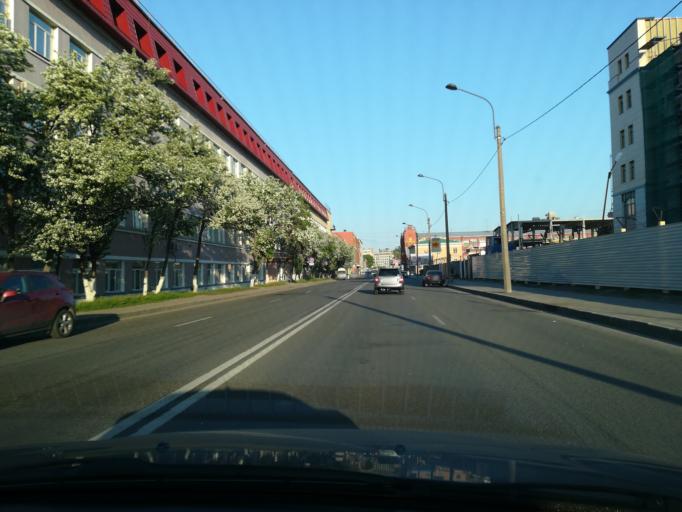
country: RU
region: St.-Petersburg
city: Vasyl'evsky Ostrov
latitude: 59.9548
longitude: 30.2558
